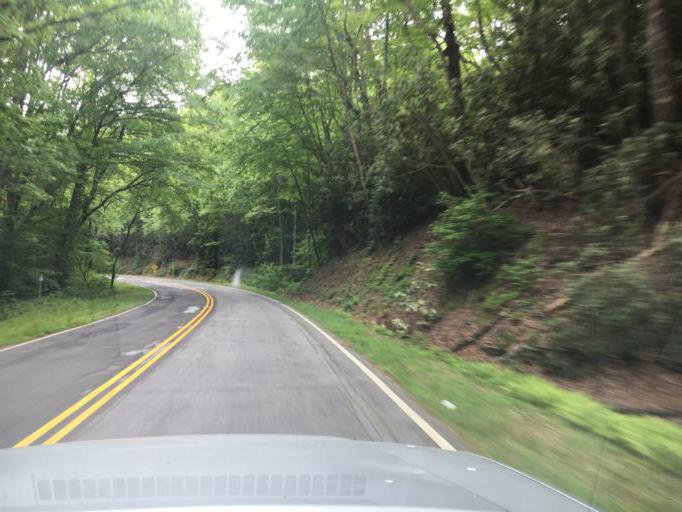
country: US
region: North Carolina
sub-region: Henderson County
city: Flat Rock
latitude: 35.1759
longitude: -82.4057
